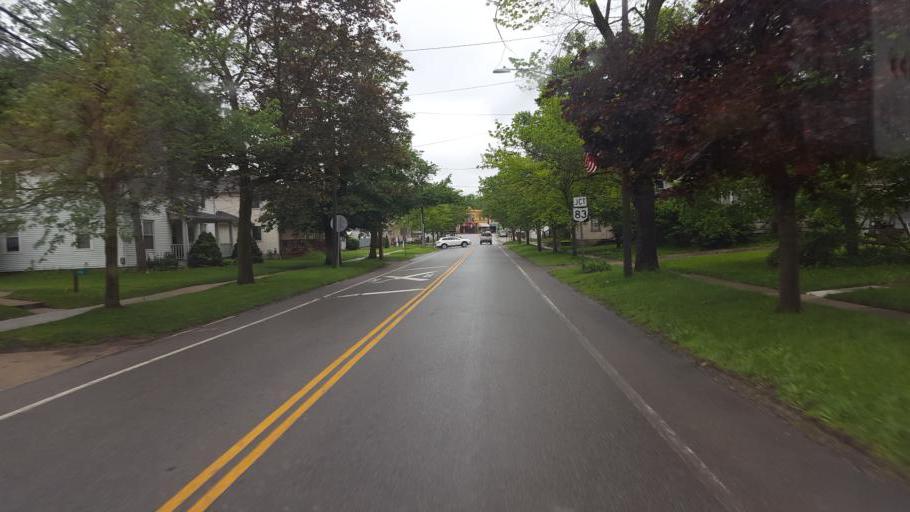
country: US
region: Ohio
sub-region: Medina County
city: Lodi
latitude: 41.0329
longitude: -82.0150
